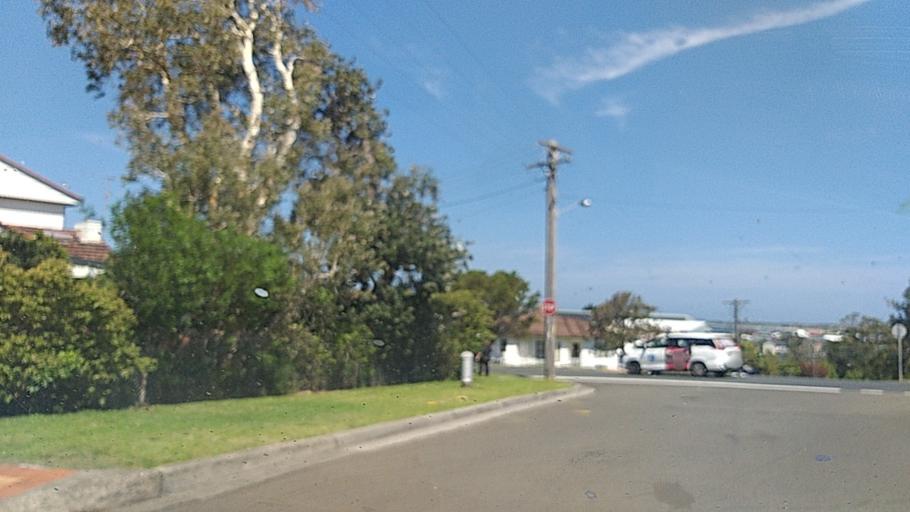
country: AU
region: New South Wales
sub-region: Wollongong
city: Bulli
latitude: -34.3437
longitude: 150.9169
